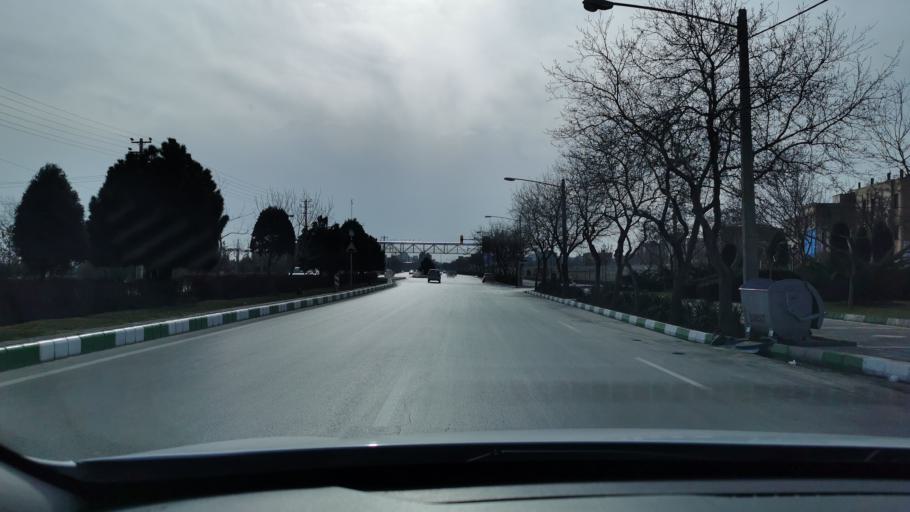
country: IR
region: Razavi Khorasan
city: Mashhad
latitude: 36.3021
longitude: 59.5177
